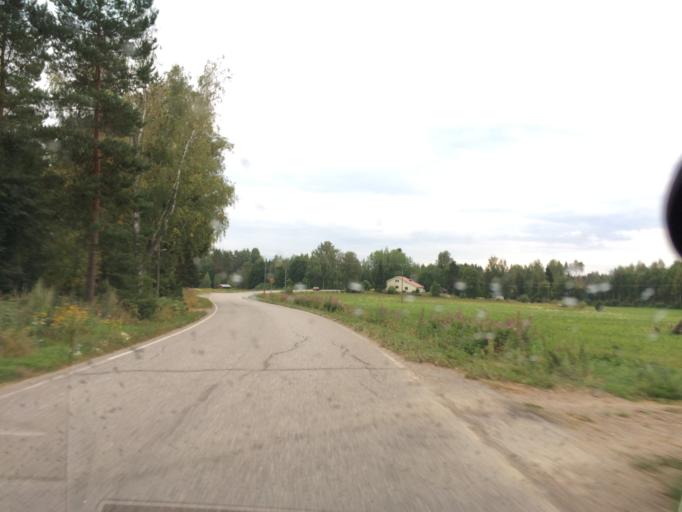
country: FI
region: Haeme
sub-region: Haemeenlinna
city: Tuulos
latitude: 61.1833
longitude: 24.7611
